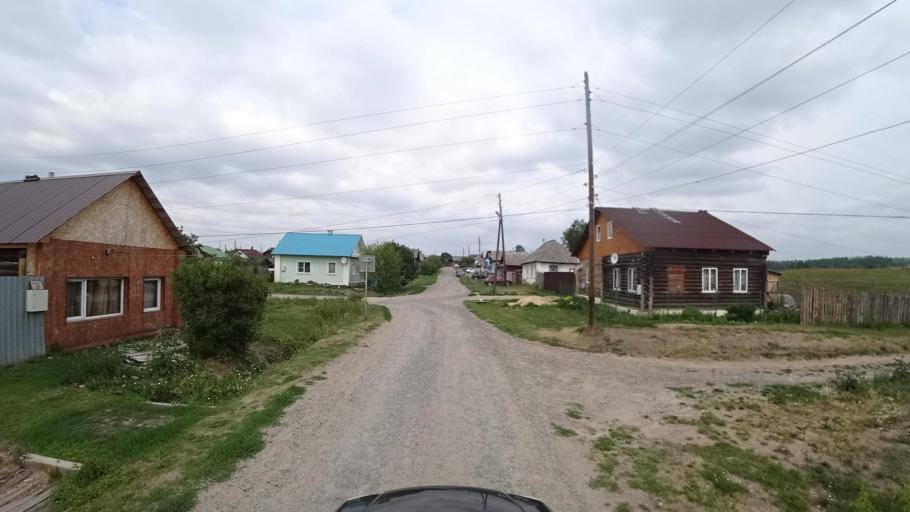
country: RU
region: Sverdlovsk
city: Kamyshlov
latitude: 56.8504
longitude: 62.6803
